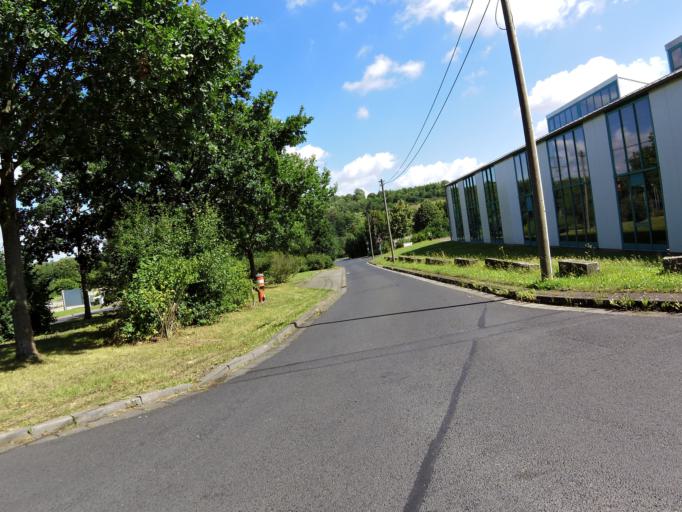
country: DE
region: Thuringia
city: Krauthausen
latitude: 51.0116
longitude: 10.2499
